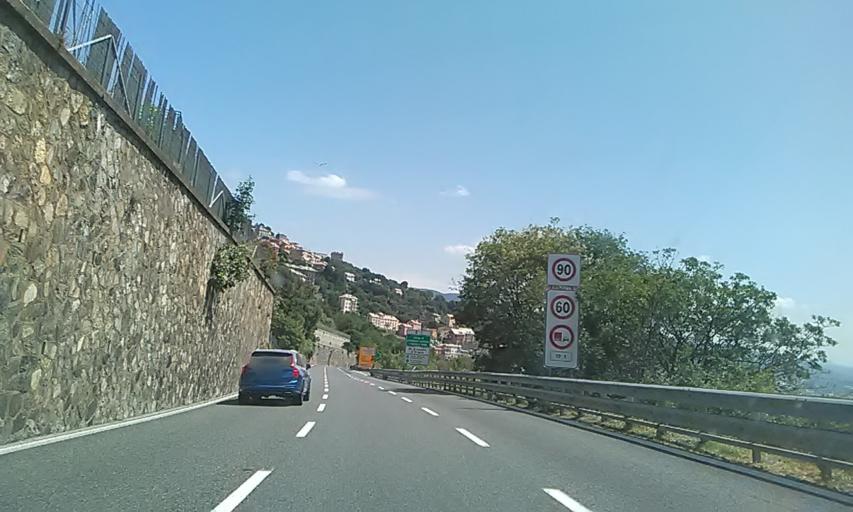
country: IT
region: Liguria
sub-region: Provincia di Genova
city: Mele
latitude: 44.4194
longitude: 8.7259
